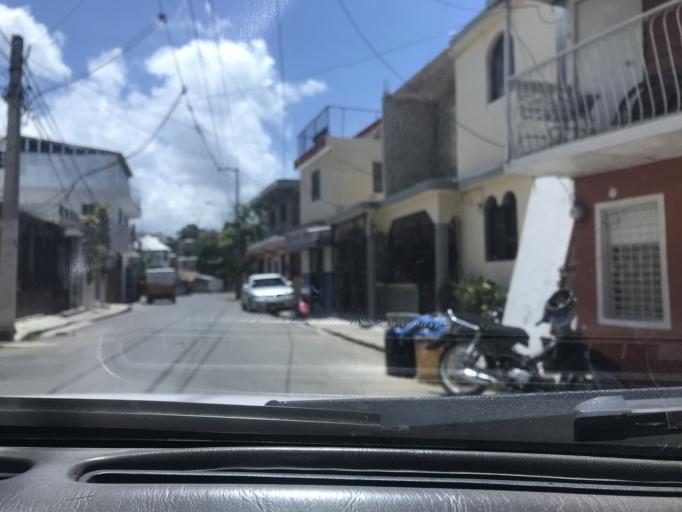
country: DO
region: Santiago
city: Santiago de los Caballeros
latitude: 19.4265
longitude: -70.6989
